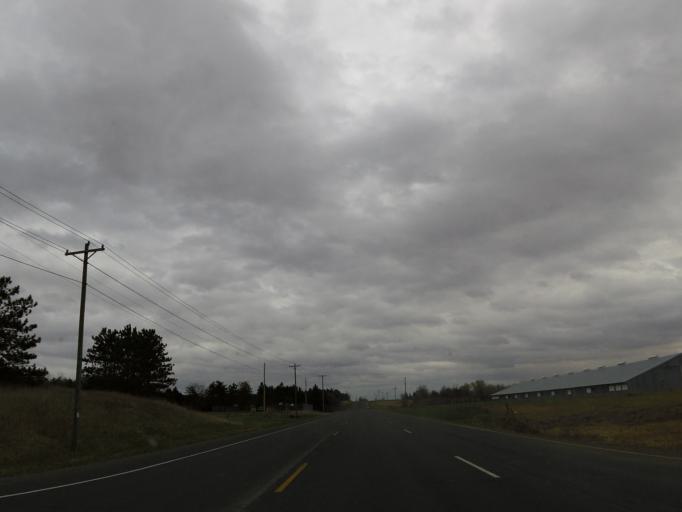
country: US
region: Wisconsin
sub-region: Saint Croix County
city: New Richmond
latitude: 45.1074
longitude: -92.5583
